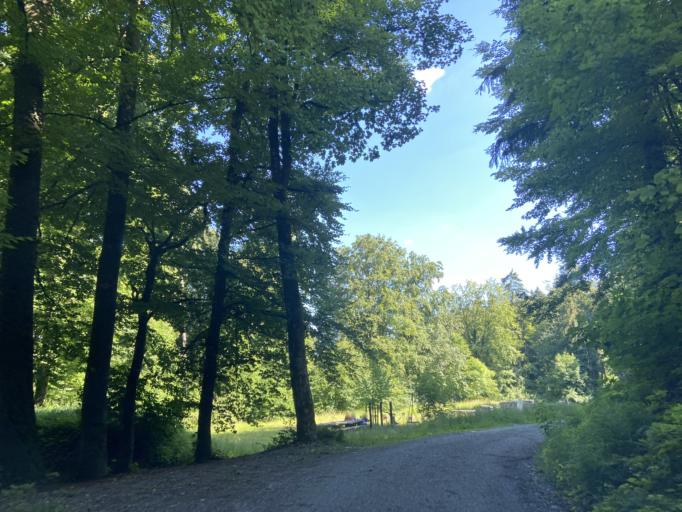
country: CH
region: Zurich
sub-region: Bezirk Winterthur
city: Wuelflingen (Kreis 6) / Niederfeld
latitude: 47.5073
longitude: 8.6656
